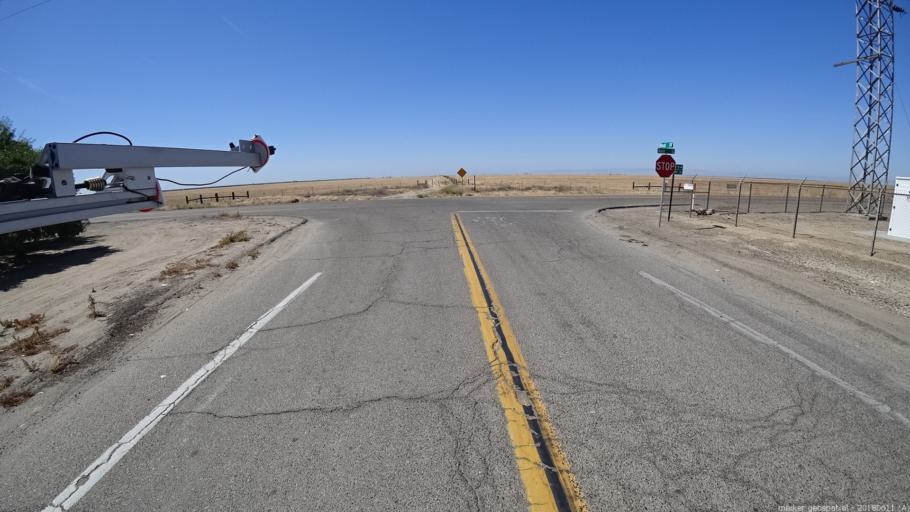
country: US
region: California
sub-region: Madera County
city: Madera
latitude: 36.9240
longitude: -120.2013
